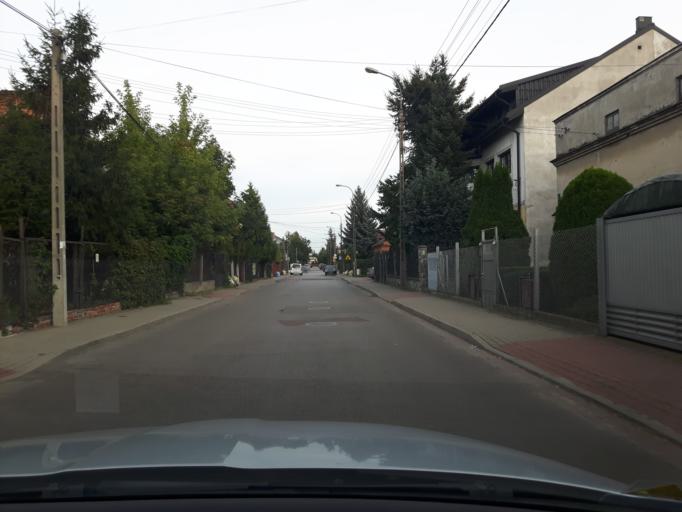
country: PL
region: Masovian Voivodeship
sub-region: Warszawa
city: Targowek
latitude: 52.2782
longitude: 21.0581
